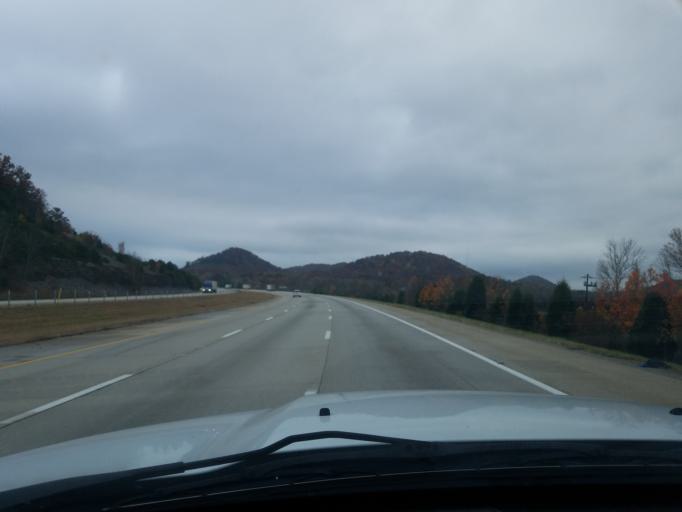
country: US
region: Kentucky
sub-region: Bullitt County
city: Lebanon Junction
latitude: 37.8981
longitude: -85.6985
